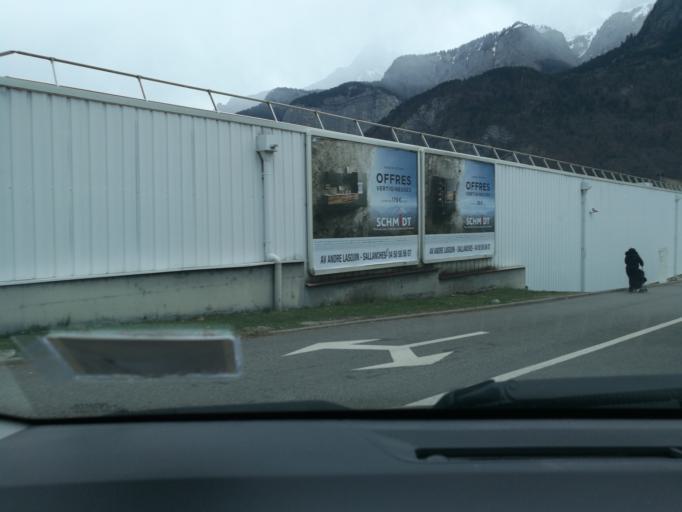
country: FR
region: Rhone-Alpes
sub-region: Departement de la Haute-Savoie
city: Sallanches
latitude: 45.9512
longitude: 6.6265
